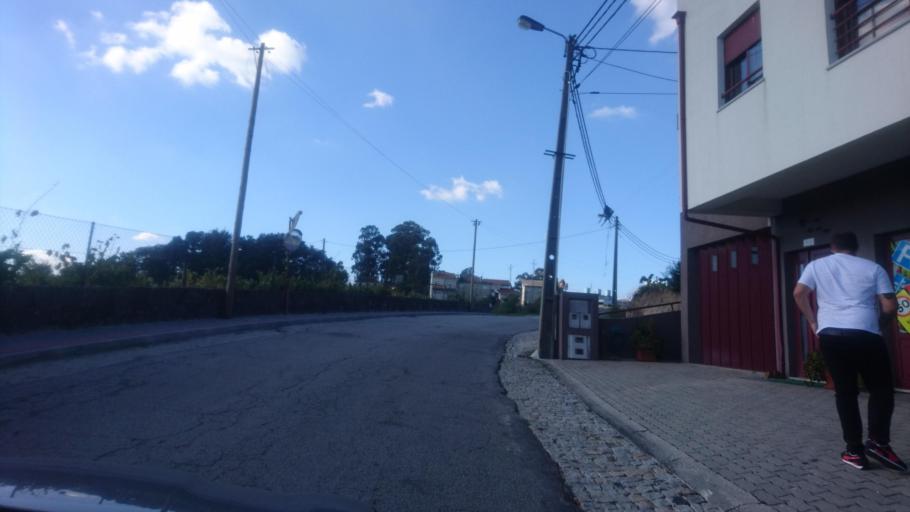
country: PT
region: Porto
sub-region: Paredes
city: Madalena
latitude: 41.2334
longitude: -8.3602
